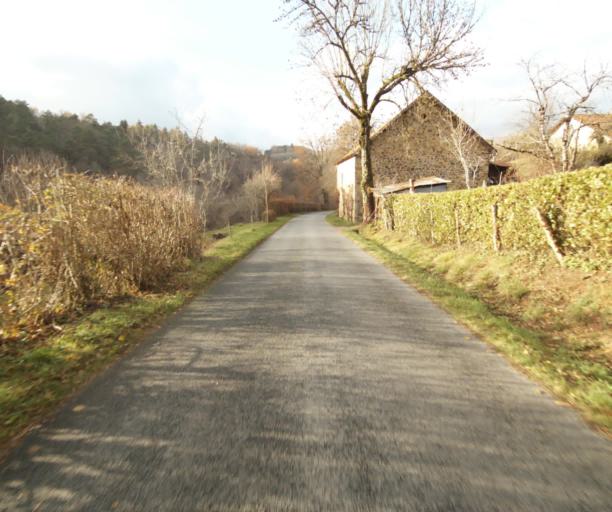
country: FR
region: Limousin
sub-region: Departement de la Correze
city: Laguenne
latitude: 45.2339
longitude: 1.7817
